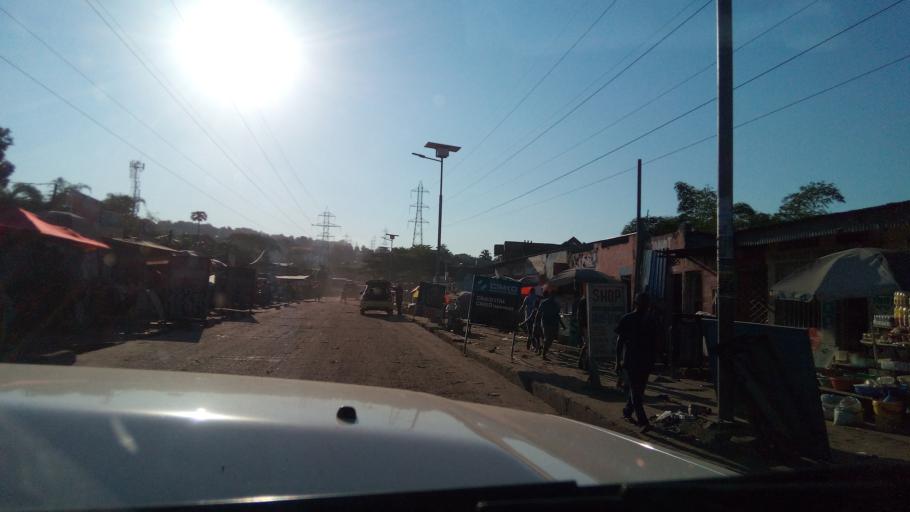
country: CD
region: Kinshasa
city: Kinshasa
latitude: -4.3581
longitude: 15.2645
